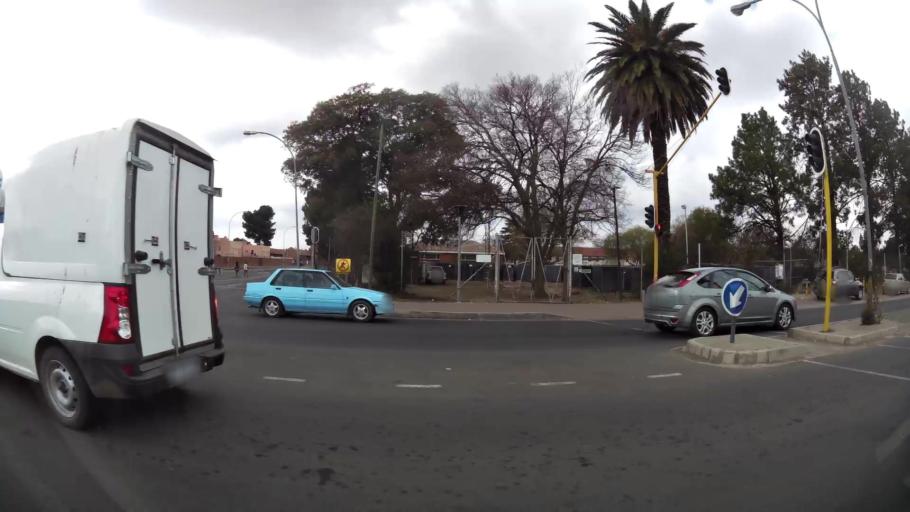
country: ZA
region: Orange Free State
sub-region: Mangaung Metropolitan Municipality
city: Bloemfontein
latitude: -29.1190
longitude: 26.2106
